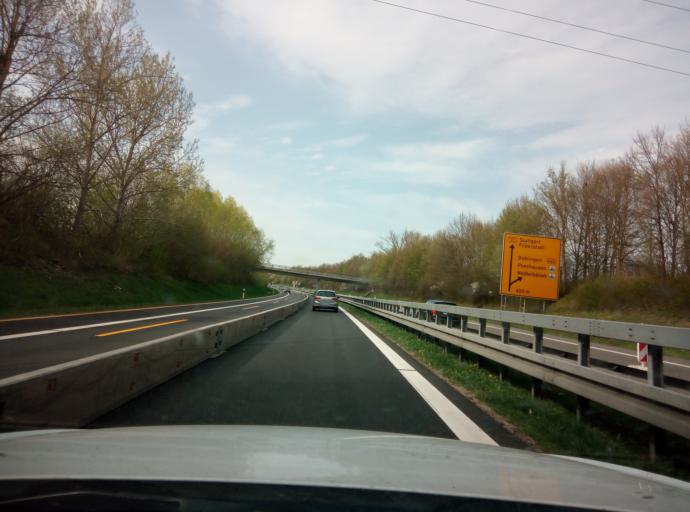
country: DE
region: Baden-Wuerttemberg
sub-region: Tuebingen Region
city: Pliezhausen
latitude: 48.5730
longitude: 9.1769
